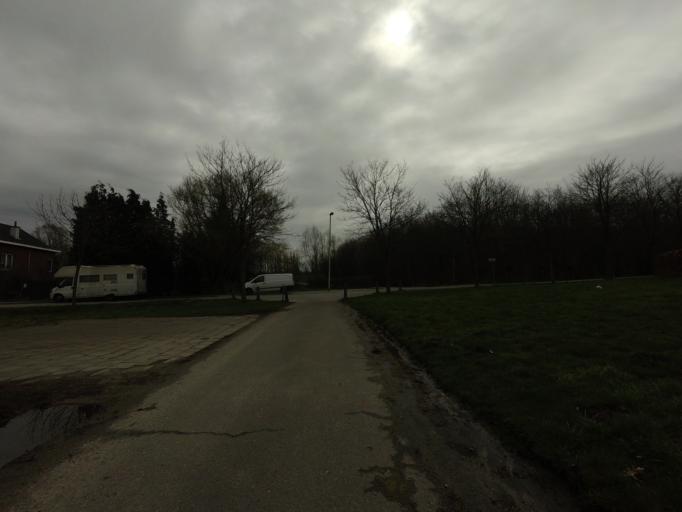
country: BE
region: Flanders
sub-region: Provincie Antwerpen
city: Lier
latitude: 51.1260
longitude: 4.5642
